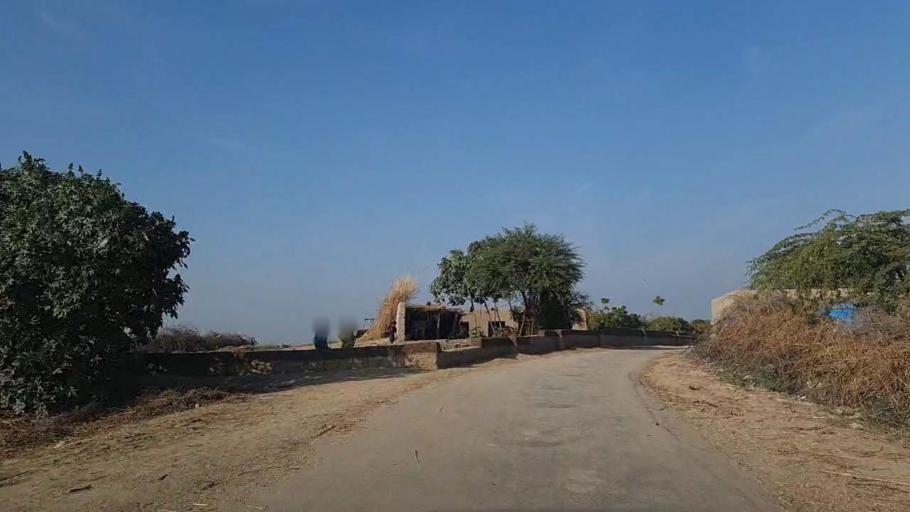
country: PK
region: Sindh
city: Nawabshah
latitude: 26.3741
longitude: 68.4761
